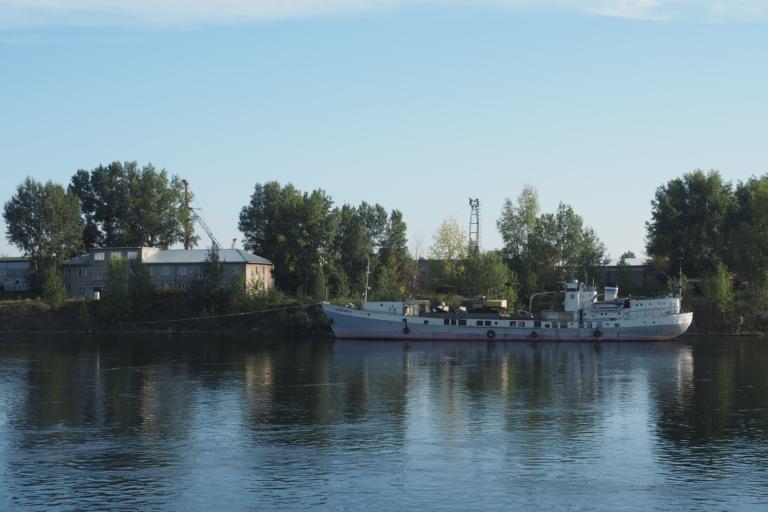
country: RU
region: Krasnoyarskiy
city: Berezovka
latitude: 56.0518
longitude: 93.1282
